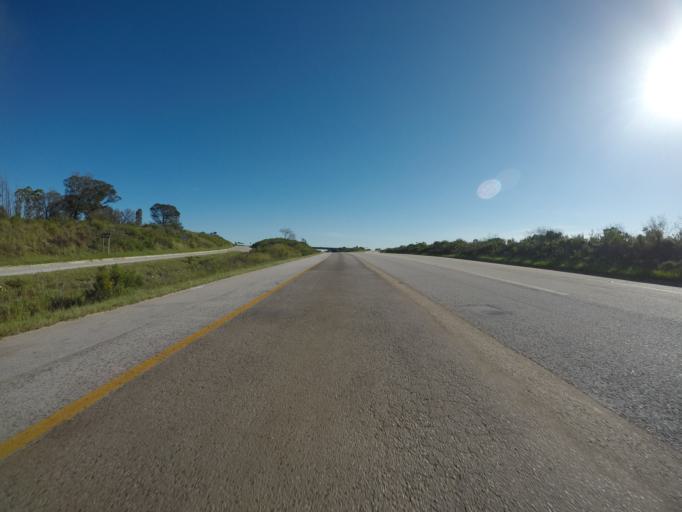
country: ZA
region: Eastern Cape
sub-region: Cacadu District Municipality
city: Jeffrey's Bay
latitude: -33.8959
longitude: 25.1243
